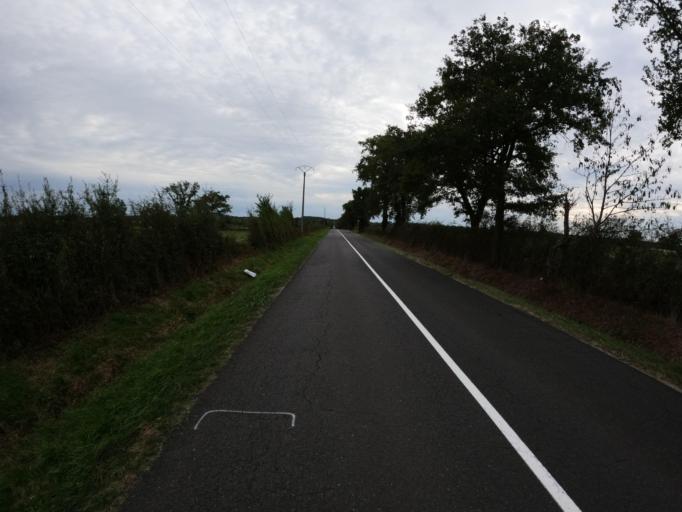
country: FR
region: Poitou-Charentes
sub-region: Departement de la Vienne
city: Saulge
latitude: 46.3652
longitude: 0.8390
